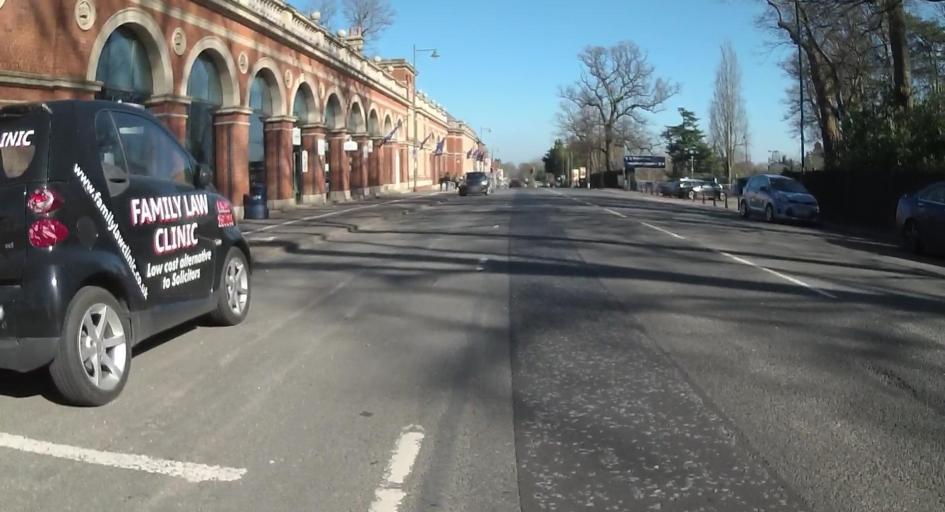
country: GB
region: England
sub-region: Royal Borough of Windsor and Maidenhead
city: Ascot
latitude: 51.4111
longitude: -0.6786
